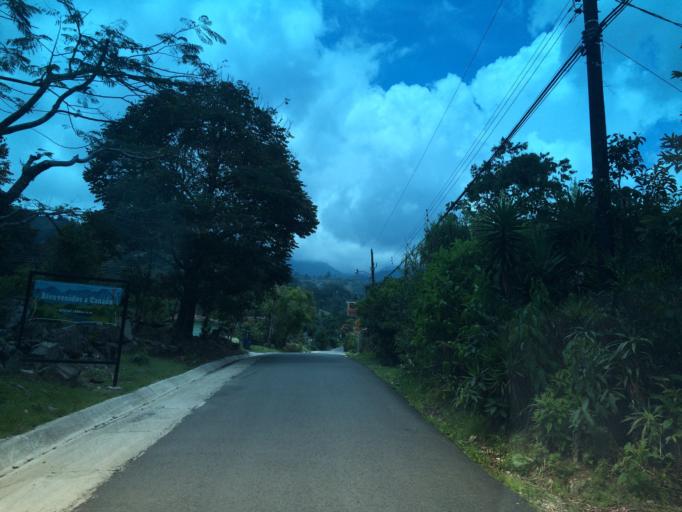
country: CR
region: San Jose
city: San Isidro
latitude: 9.4531
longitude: -83.6077
